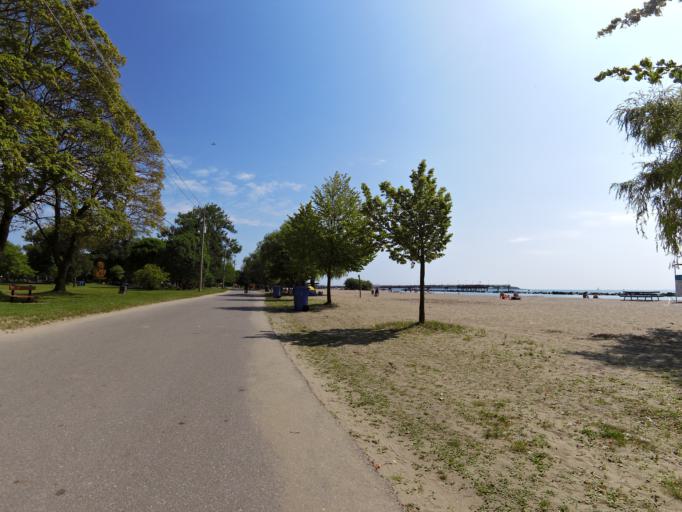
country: CA
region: Ontario
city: Toronto
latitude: 43.6157
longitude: -79.3750
